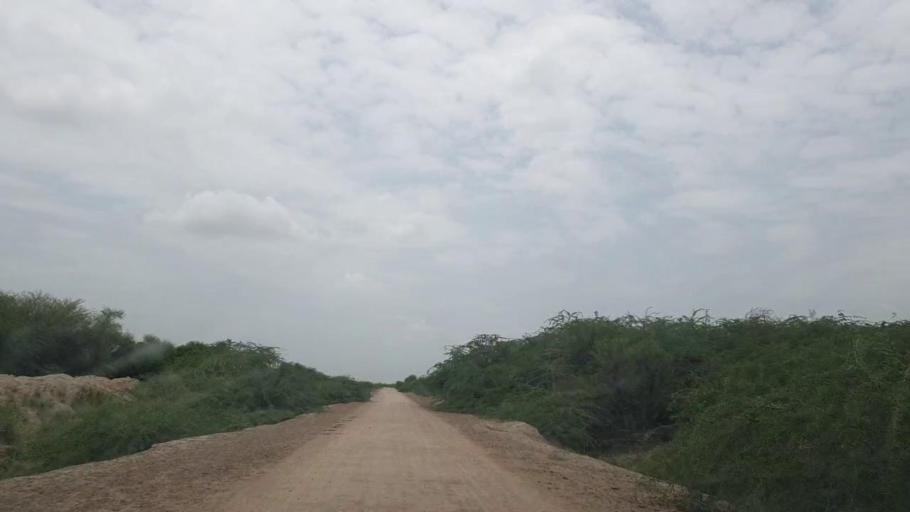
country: PK
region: Sindh
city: Naukot
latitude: 24.9302
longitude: 69.1790
